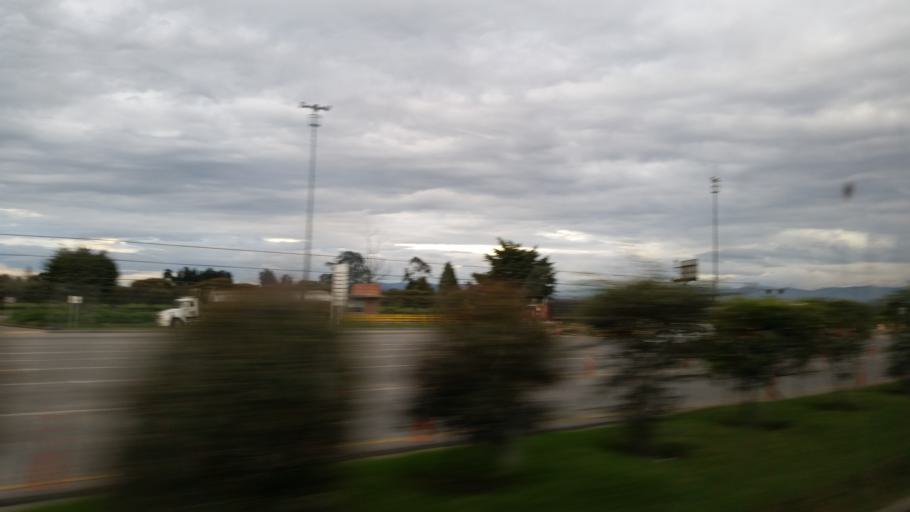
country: CO
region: Cundinamarca
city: Funza
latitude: 4.6980
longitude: -74.1788
